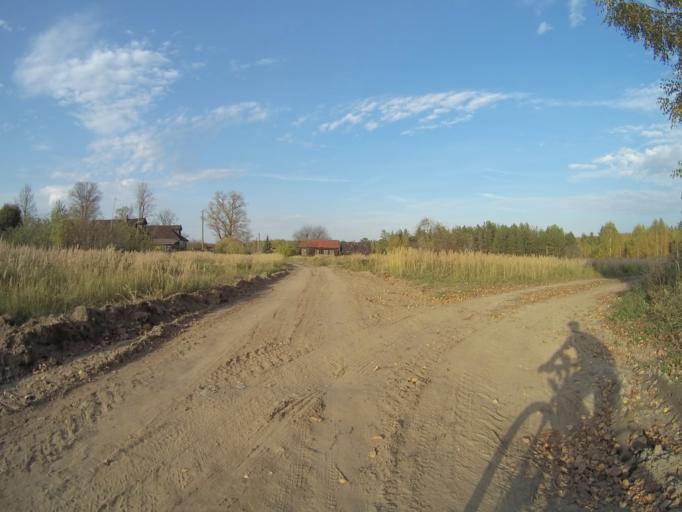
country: RU
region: Vladimir
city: Sobinka
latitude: 55.8119
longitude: 40.0686
